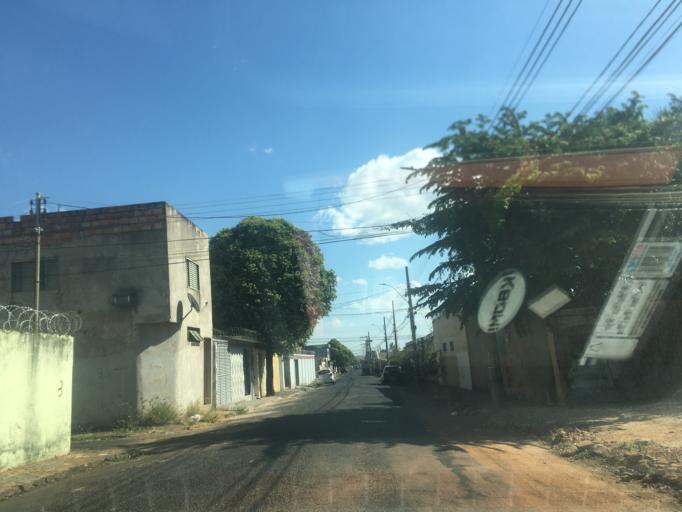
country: BR
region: Minas Gerais
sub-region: Uberlandia
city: Uberlandia
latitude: -18.9040
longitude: -48.2798
